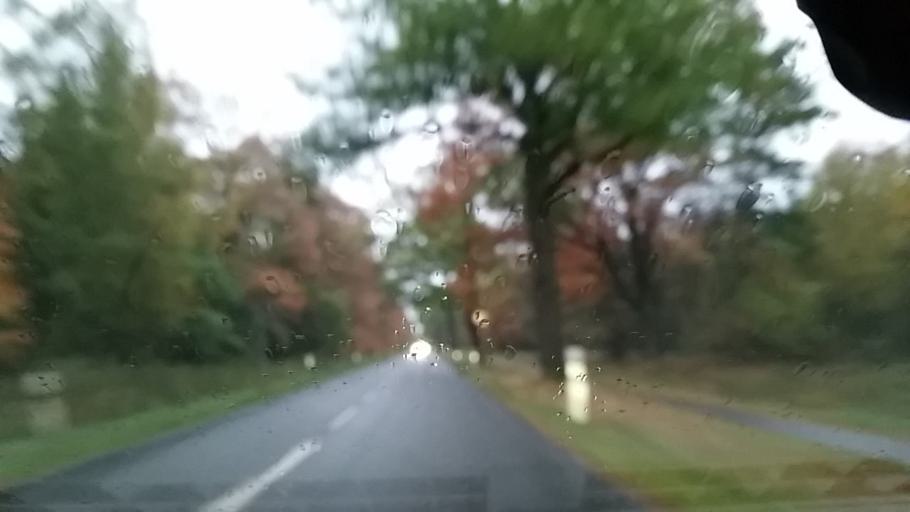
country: DE
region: Lower Saxony
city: Weyhausen
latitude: 52.4459
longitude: 10.7133
